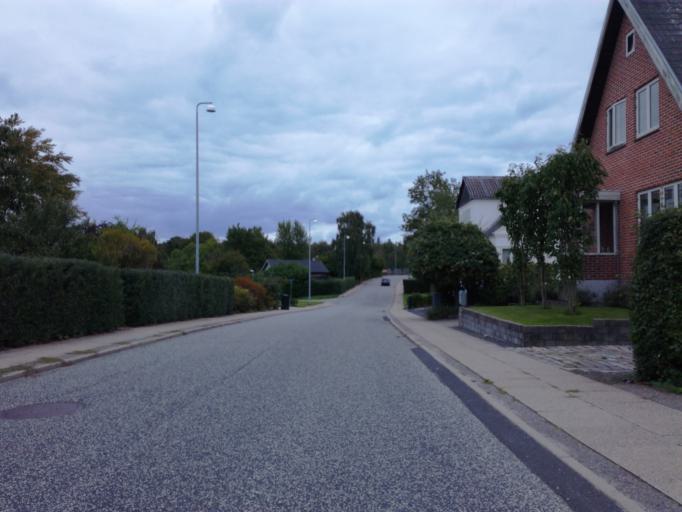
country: DK
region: South Denmark
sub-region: Vejle Kommune
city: Vejle
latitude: 55.6871
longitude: 9.5611
